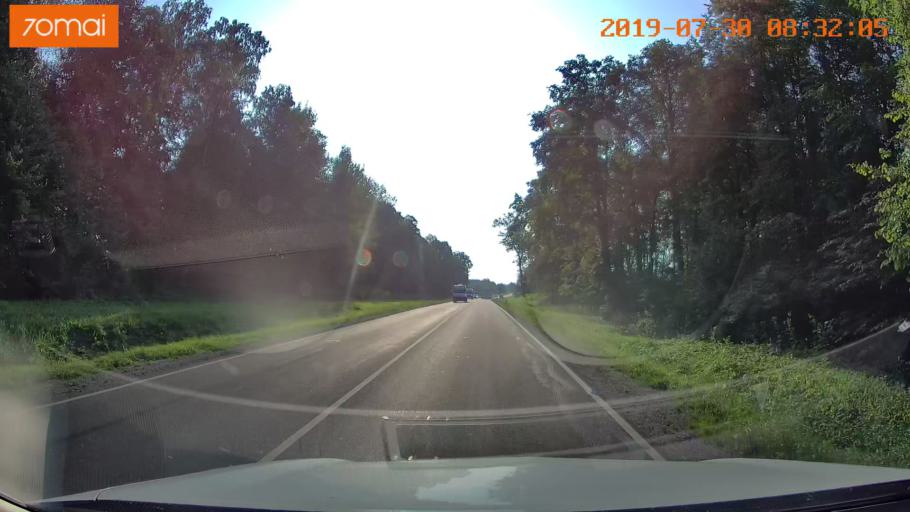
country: RU
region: Kaliningrad
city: Chernyakhovsk
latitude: 54.6385
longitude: 21.7217
